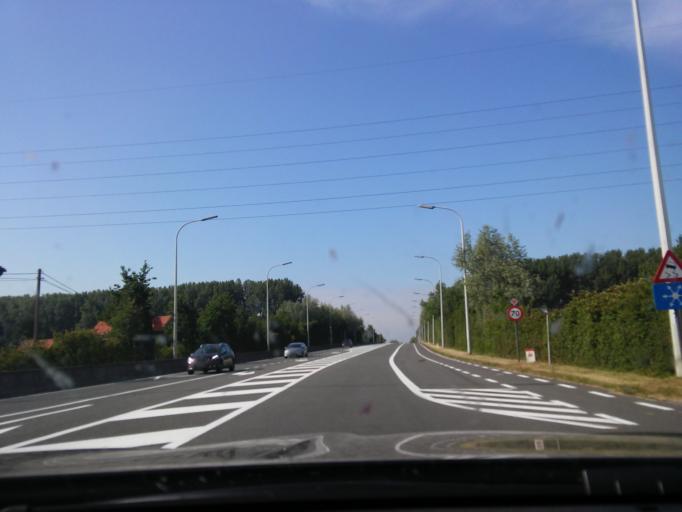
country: BE
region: Flanders
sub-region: Provincie Oost-Vlaanderen
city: Maldegem
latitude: 51.2306
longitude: 3.4468
